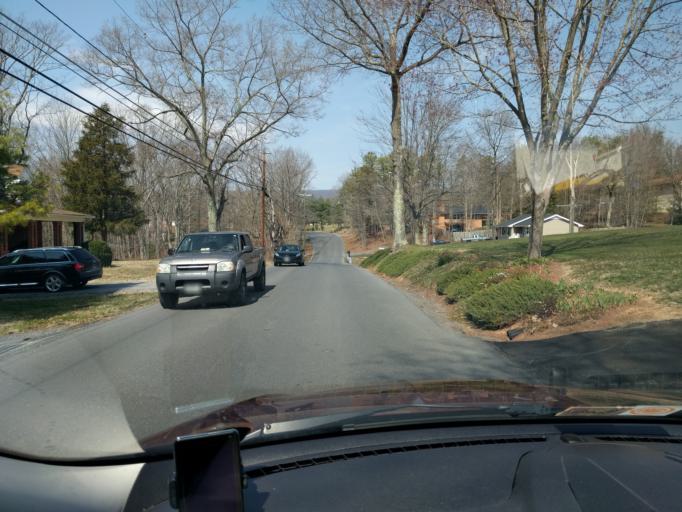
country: US
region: Virginia
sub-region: Alleghany County
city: Clifton Forge
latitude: 37.8230
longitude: -79.8135
